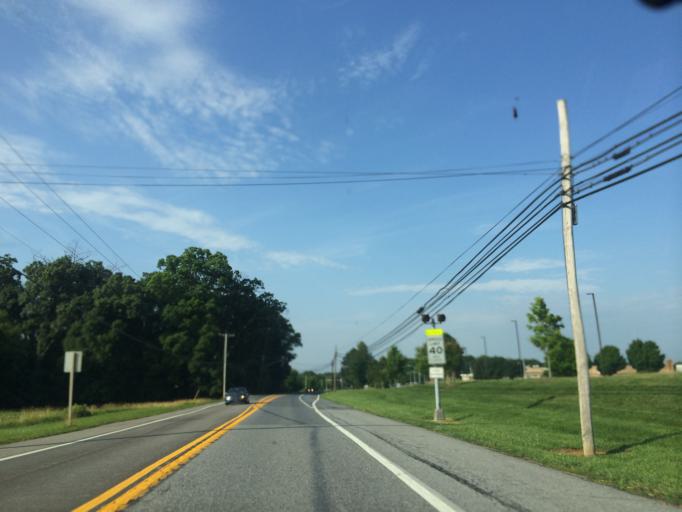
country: US
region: Maryland
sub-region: Carroll County
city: Sykesville
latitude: 39.3006
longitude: -77.0207
